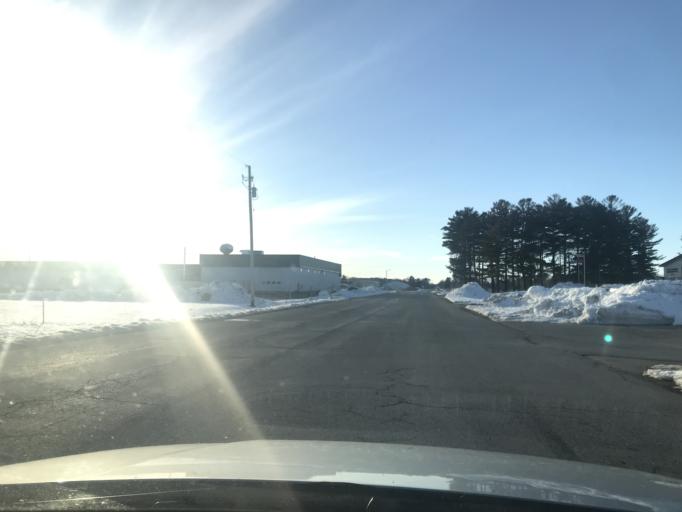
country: US
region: Wisconsin
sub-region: Marinette County
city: Peshtigo
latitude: 45.0551
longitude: -87.7306
